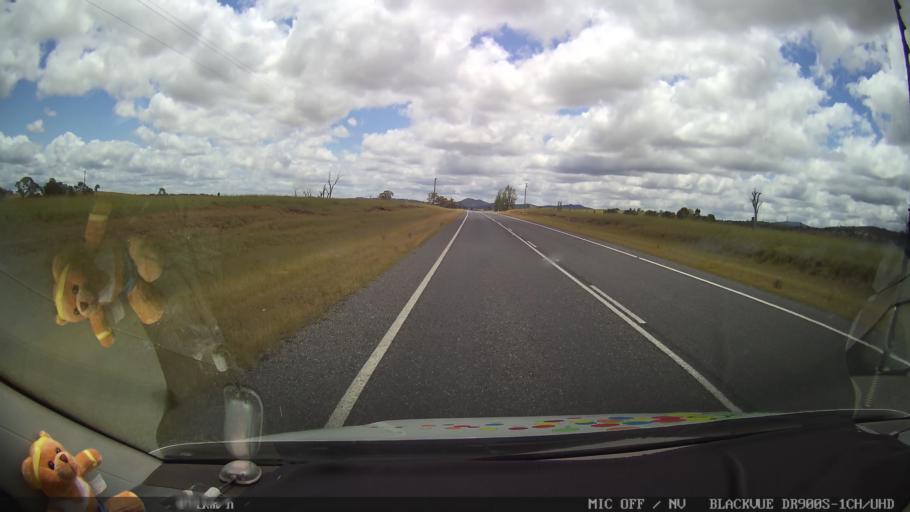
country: AU
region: New South Wales
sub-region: Glen Innes Severn
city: Glen Innes
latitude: -29.4163
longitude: 151.8643
